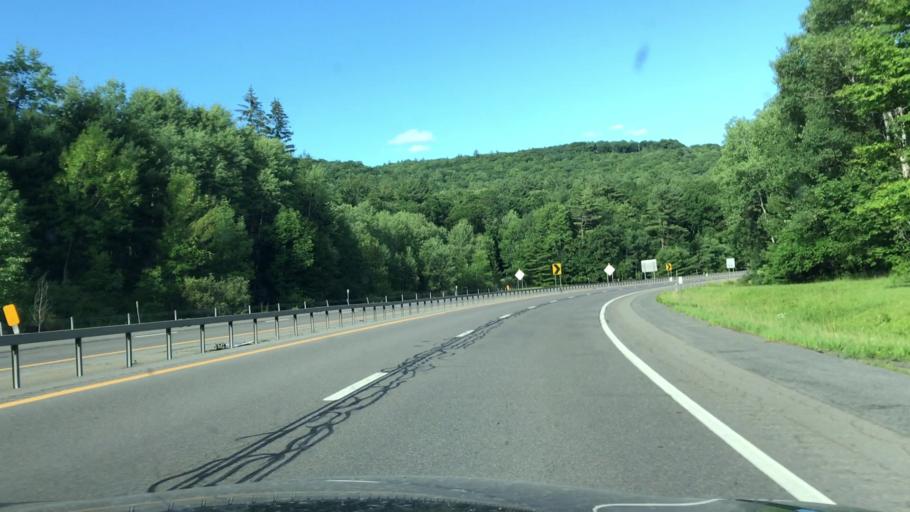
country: US
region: New York
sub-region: Delaware County
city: Hancock
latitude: 41.9599
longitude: -75.2840
